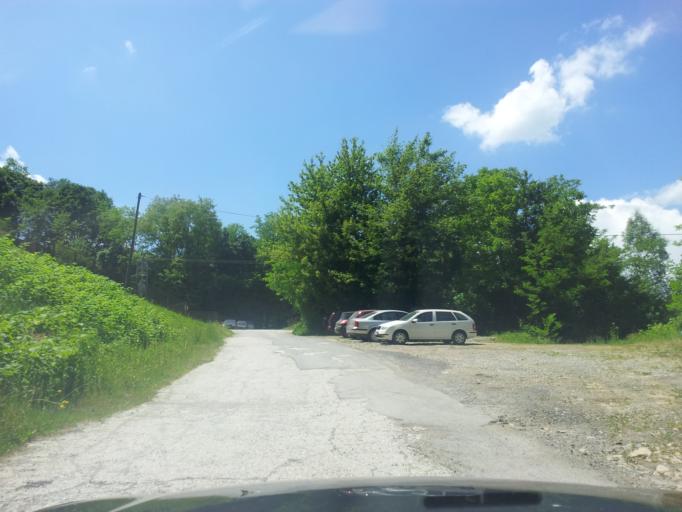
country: HR
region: Karlovacka
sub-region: Grad Karlovac
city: Karlovac
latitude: 45.4587
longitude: 15.5258
